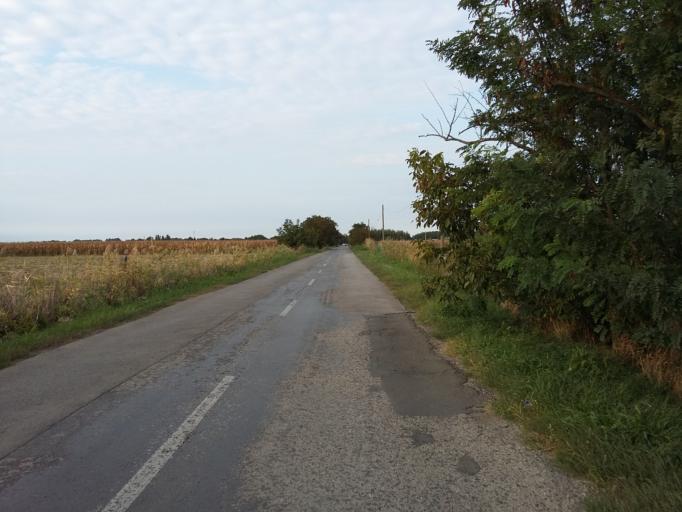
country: HU
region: Csongrad
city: Szeged
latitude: 46.2117
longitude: 20.1084
